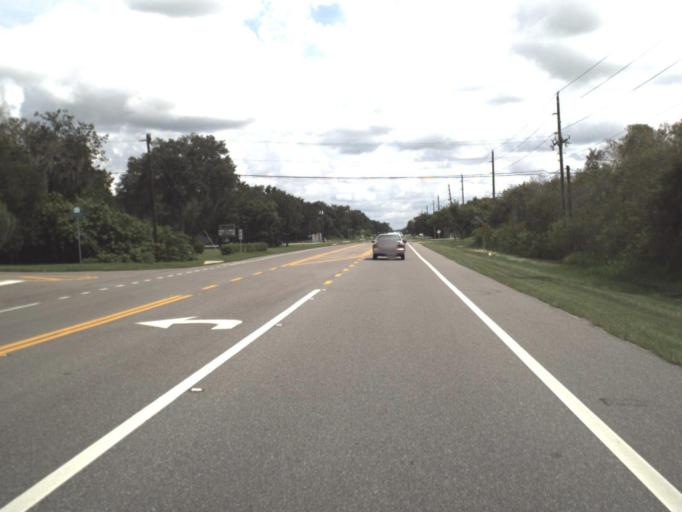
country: US
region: Florida
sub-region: Sarasota County
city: Lake Sarasota
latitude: 27.2664
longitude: -82.4153
